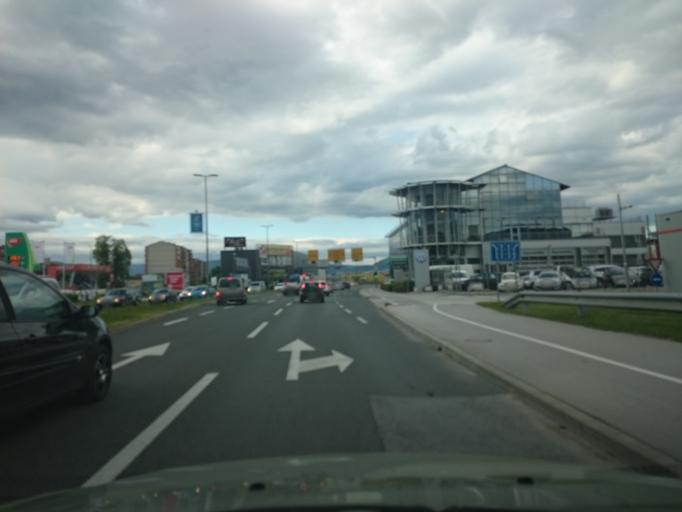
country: SI
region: Celje
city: Trnovlje pri Celju
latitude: 46.2443
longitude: 15.2779
